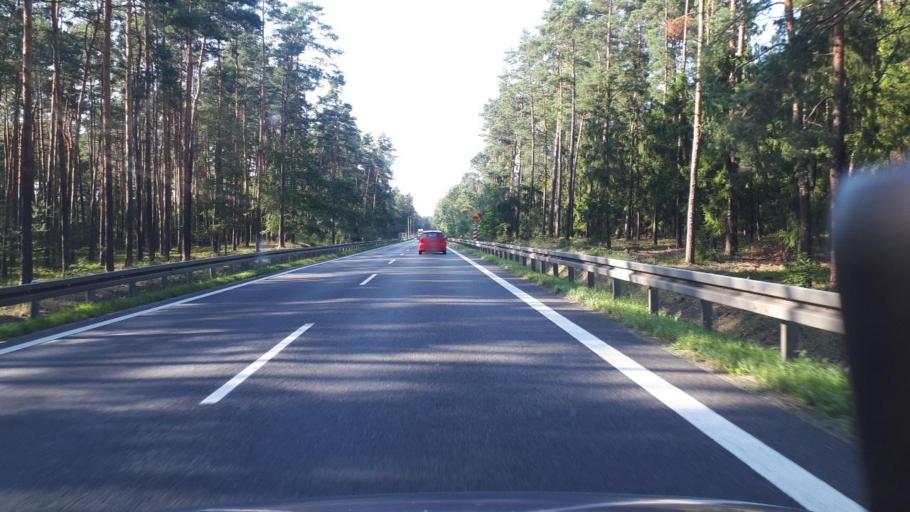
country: PL
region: Silesian Voivodeship
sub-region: Powiat lubliniecki
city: Lubliniec
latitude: 50.6165
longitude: 18.6894
